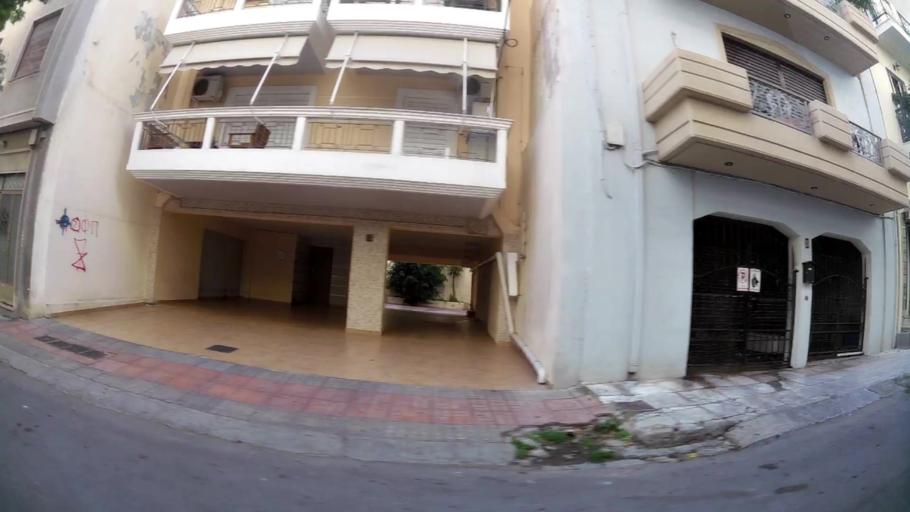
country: GR
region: Attica
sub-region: Nomos Piraios
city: Drapetsona
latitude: 37.9499
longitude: 23.6272
